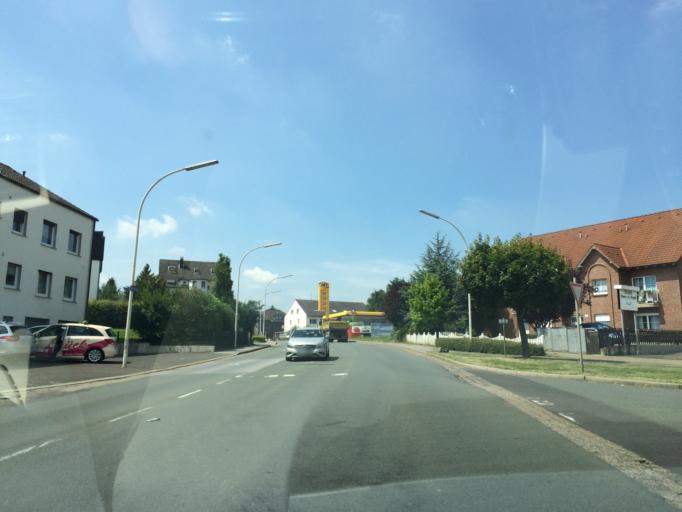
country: DE
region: North Rhine-Westphalia
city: Hemer
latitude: 51.3749
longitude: 7.7475
